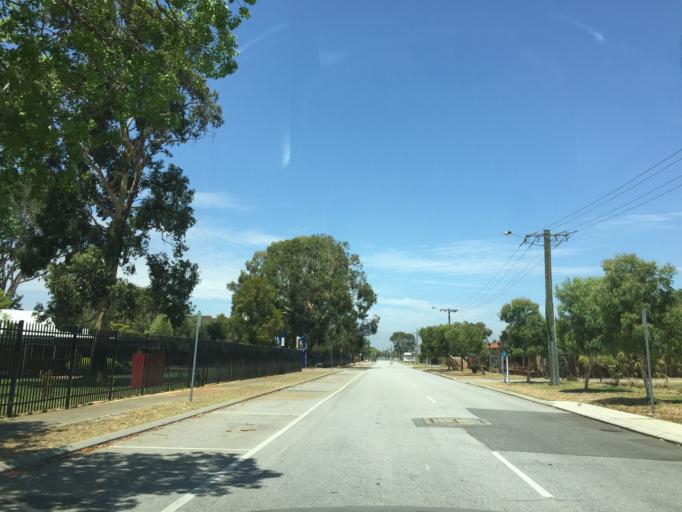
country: AU
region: Western Australia
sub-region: Canning
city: Queens Park
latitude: -32.0035
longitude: 115.9396
